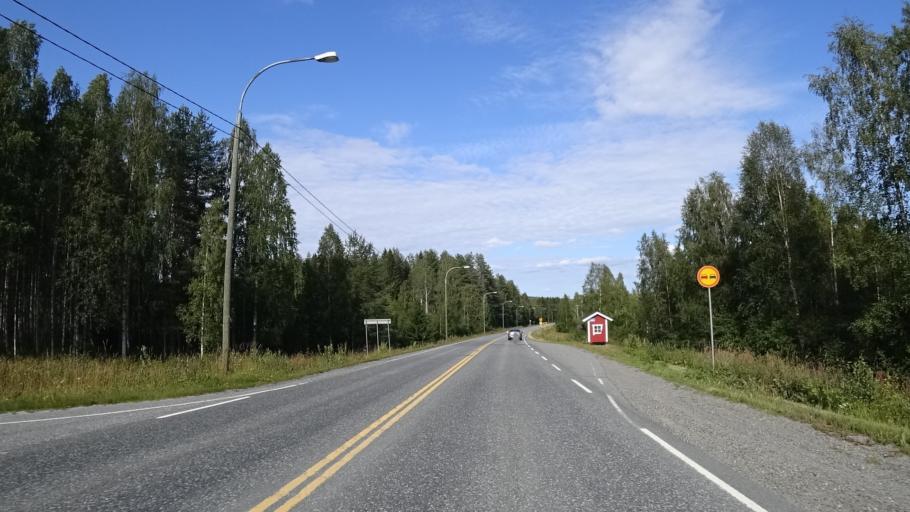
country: FI
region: North Karelia
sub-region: Joensuu
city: Eno
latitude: 62.7918
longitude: 30.0851
